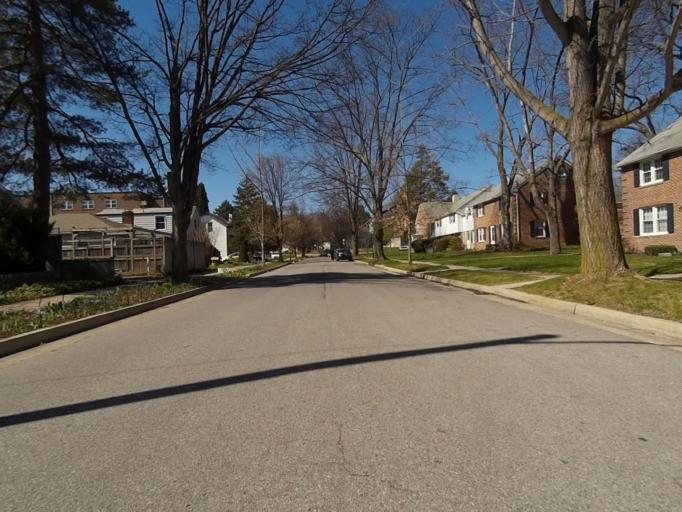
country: US
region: Pennsylvania
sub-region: Centre County
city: State College
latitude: 40.7885
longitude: -77.8505
